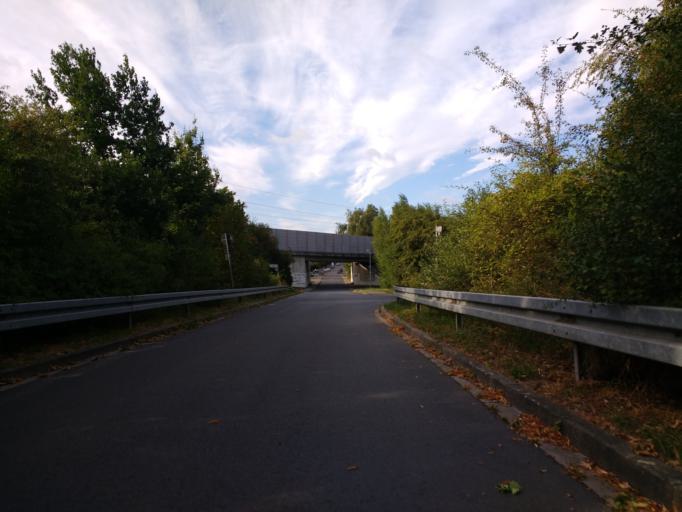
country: DE
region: Lower Saxony
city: Osloss
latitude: 52.4209
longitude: 10.6861
